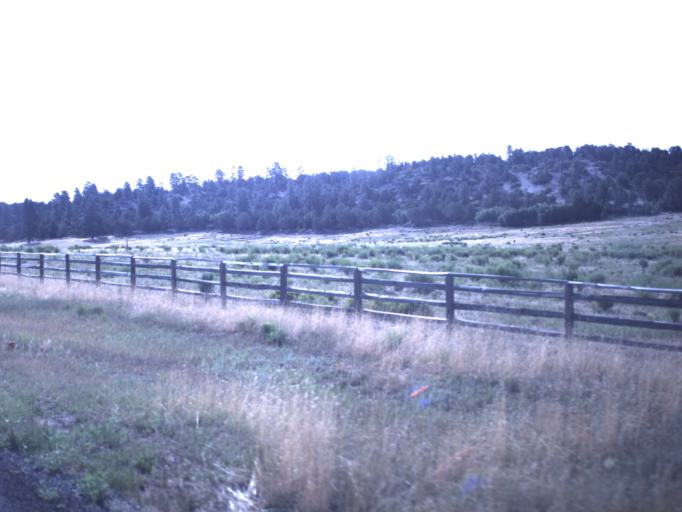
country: US
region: Utah
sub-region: Washington County
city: Hildale
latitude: 37.2408
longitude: -112.8228
